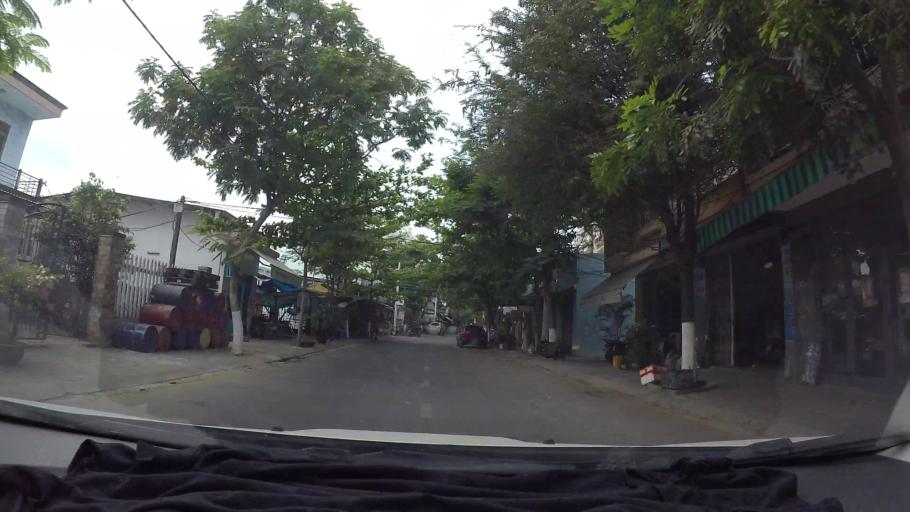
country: VN
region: Da Nang
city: Thanh Khe
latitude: 16.0555
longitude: 108.1785
